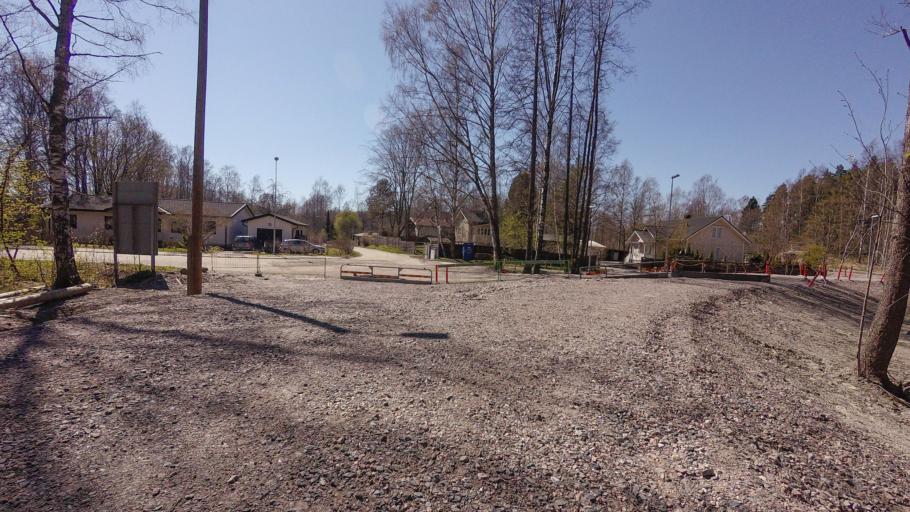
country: FI
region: Uusimaa
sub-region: Helsinki
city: Vantaa
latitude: 60.2228
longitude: 25.1279
